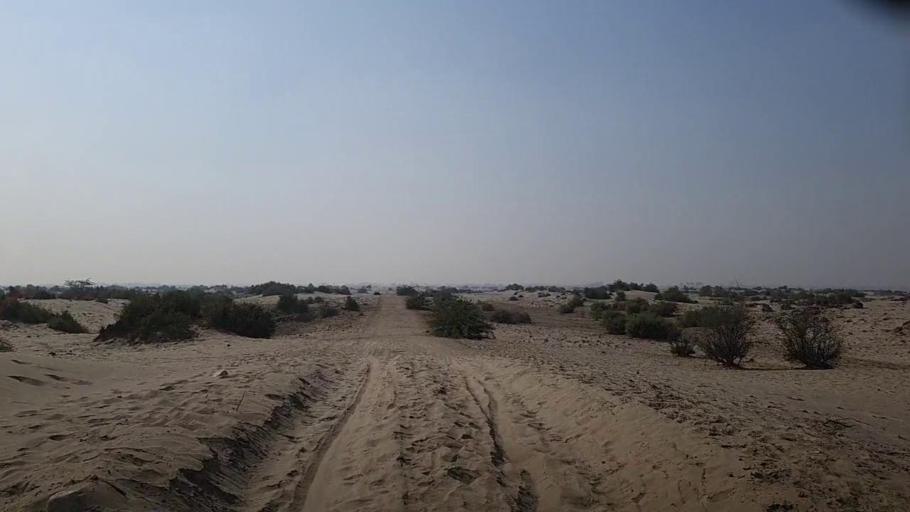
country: PK
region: Sindh
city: Bozdar
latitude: 27.2268
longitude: 68.5892
